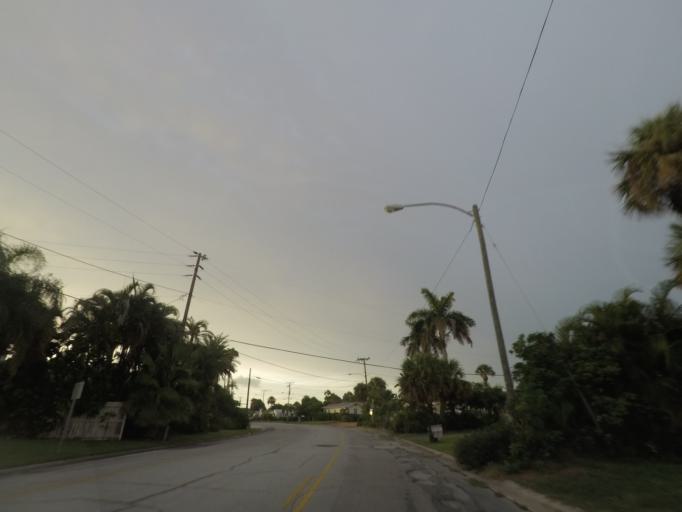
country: US
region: Florida
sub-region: Pinellas County
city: Saint Pete Beach
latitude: 27.7389
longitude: -82.7482
